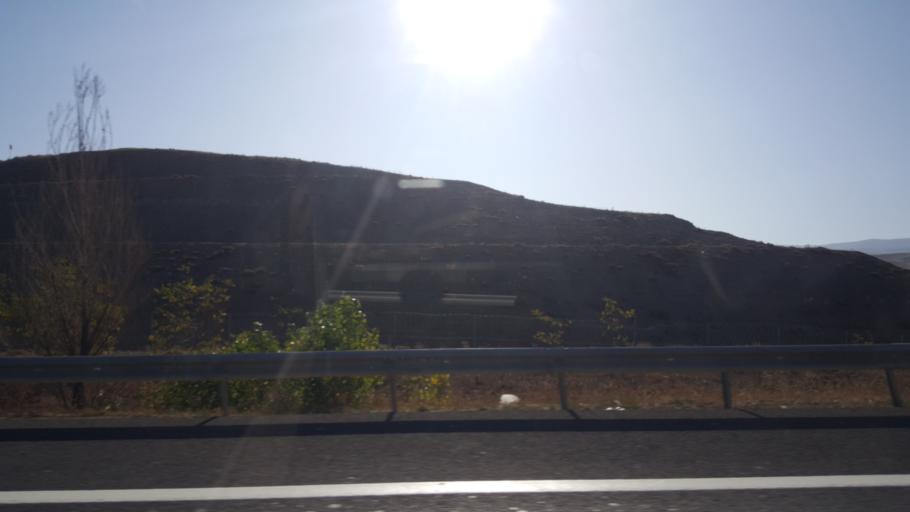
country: TR
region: Ankara
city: Mamak
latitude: 39.8963
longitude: 32.9616
